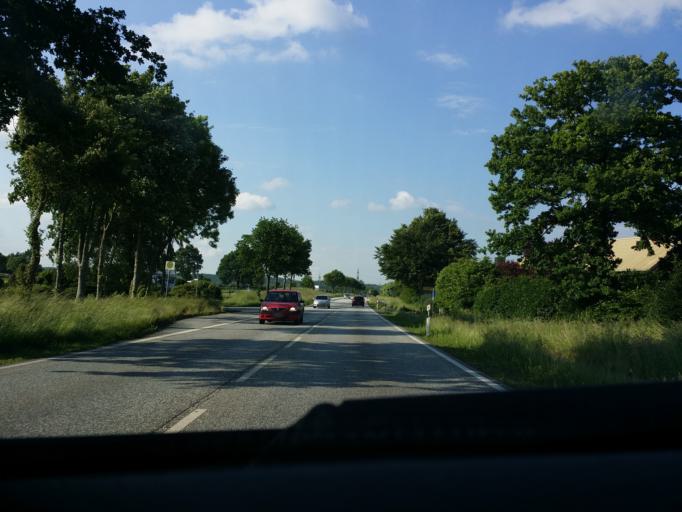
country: DE
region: Schleswig-Holstein
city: Borgstedt
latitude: 54.3344
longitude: 9.6963
